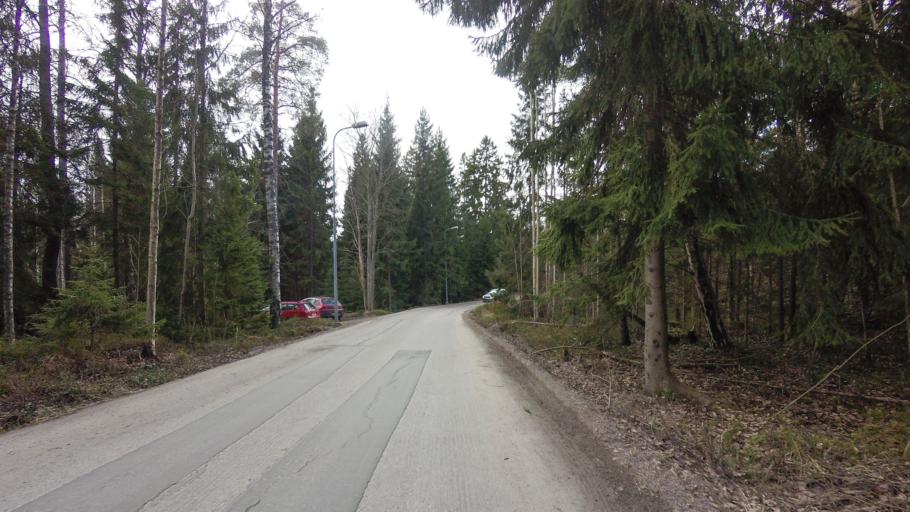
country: FI
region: Uusimaa
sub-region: Helsinki
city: Vantaa
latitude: 60.1926
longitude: 25.1012
